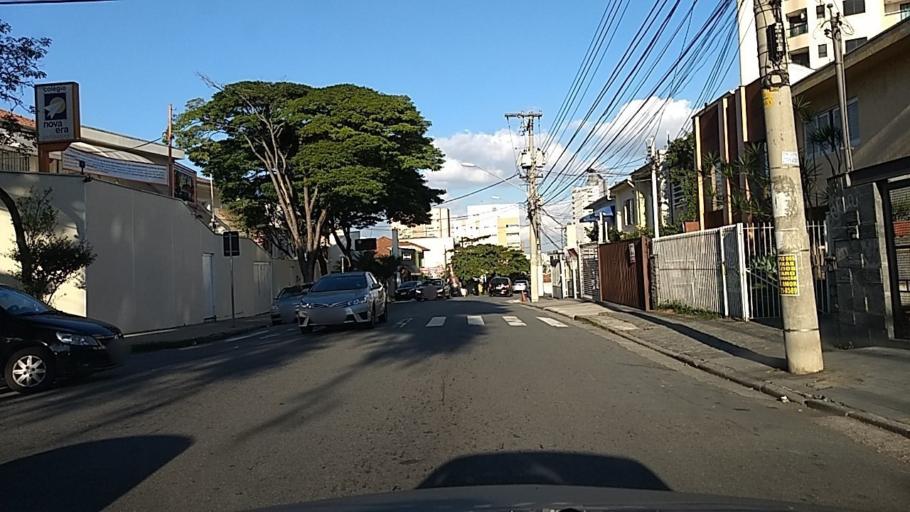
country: BR
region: Sao Paulo
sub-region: Sao Paulo
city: Sao Paulo
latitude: -23.4860
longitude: -46.6156
